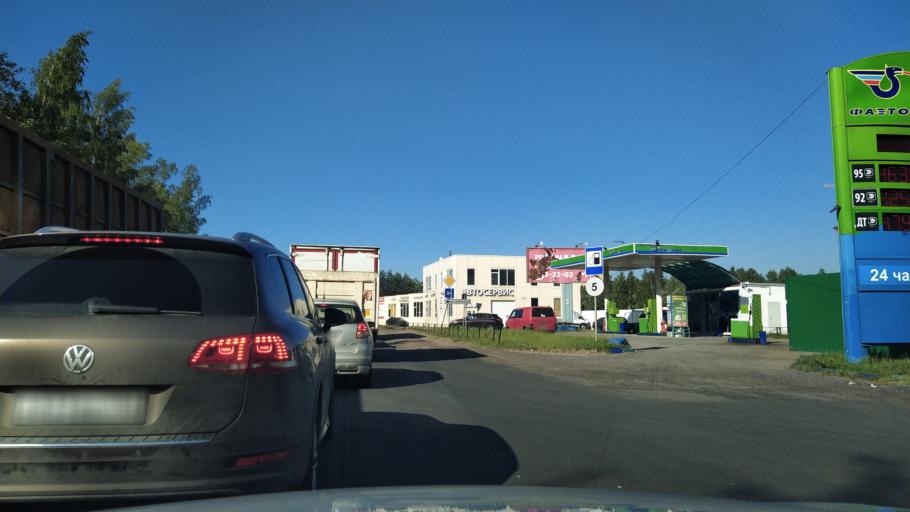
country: RU
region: Leningrad
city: Murino
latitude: 60.0481
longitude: 30.4644
